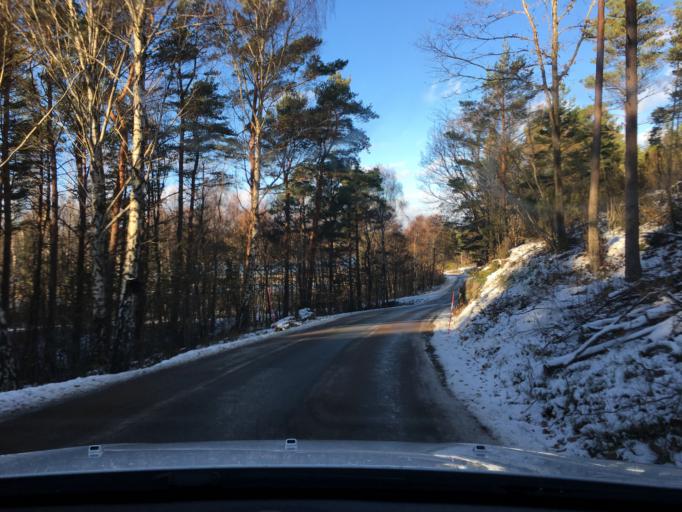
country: SE
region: Vaestra Goetaland
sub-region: Tjorns Kommun
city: Myggenas
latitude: 58.0935
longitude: 11.7351
